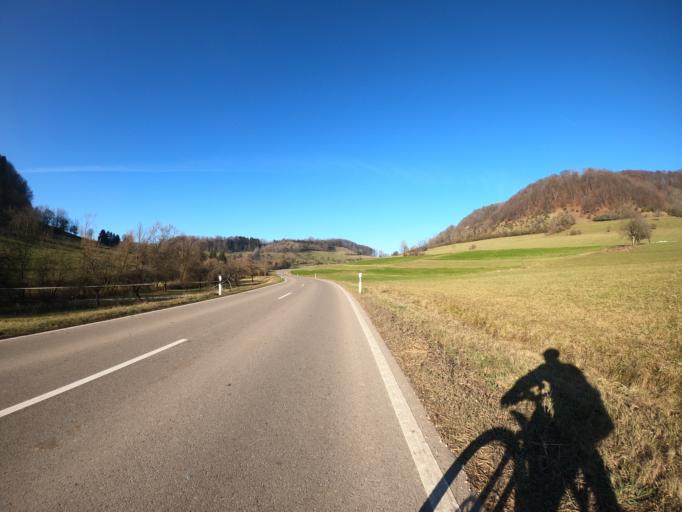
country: DE
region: Baden-Wuerttemberg
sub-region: Regierungsbezirk Stuttgart
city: Eschenbach
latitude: 48.6207
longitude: 9.6784
